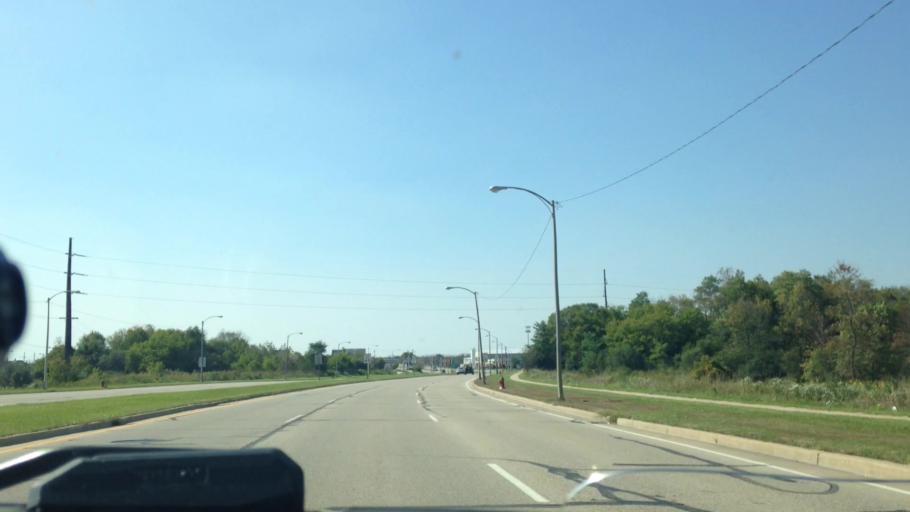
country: US
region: Wisconsin
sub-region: Milwaukee County
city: Brown Deer
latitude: 43.1777
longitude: -88.0368
